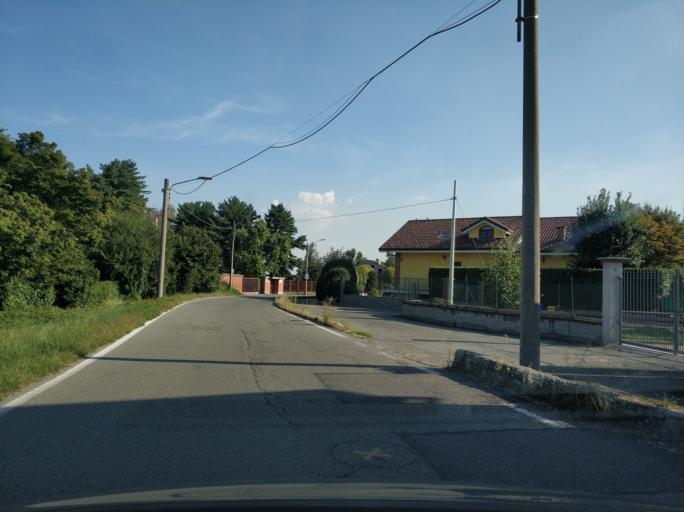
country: IT
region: Piedmont
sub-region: Provincia di Torino
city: San Maurizio
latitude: 45.2091
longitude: 7.6291
